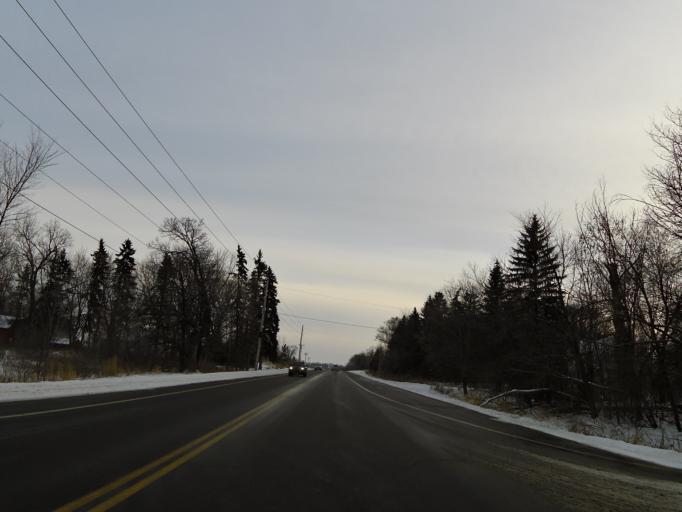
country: US
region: Minnesota
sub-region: Carver County
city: Victoria
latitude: 44.8448
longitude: -93.6544
